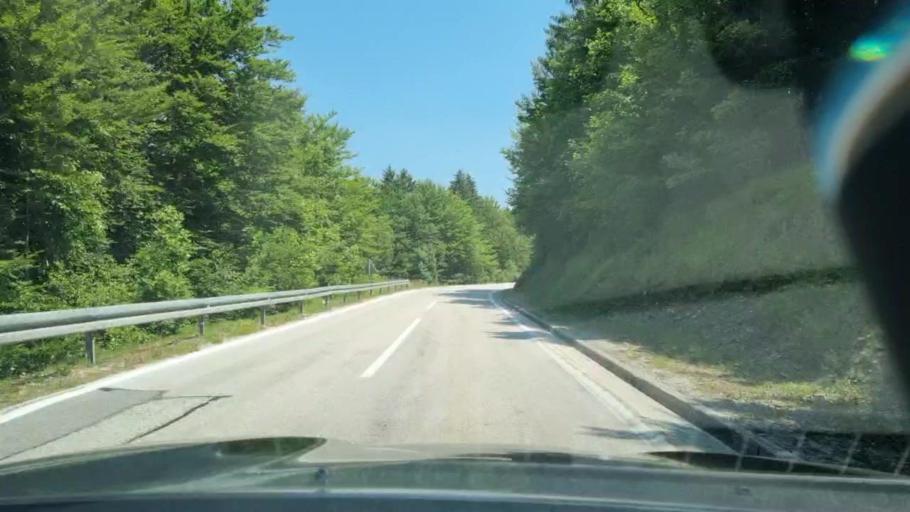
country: BA
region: Federation of Bosnia and Herzegovina
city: Sanica
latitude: 44.5042
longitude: 16.3653
